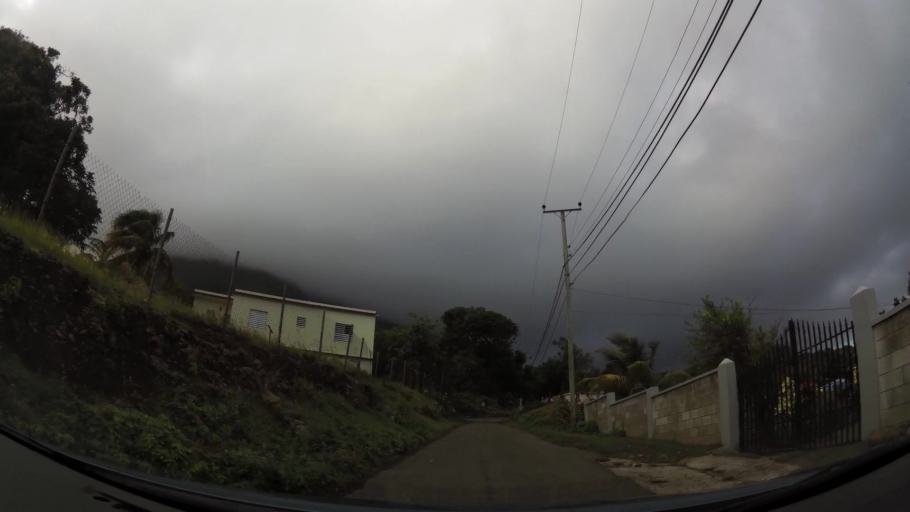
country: KN
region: Saint George Gingerland
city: Market Shop
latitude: 17.1397
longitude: -62.5738
